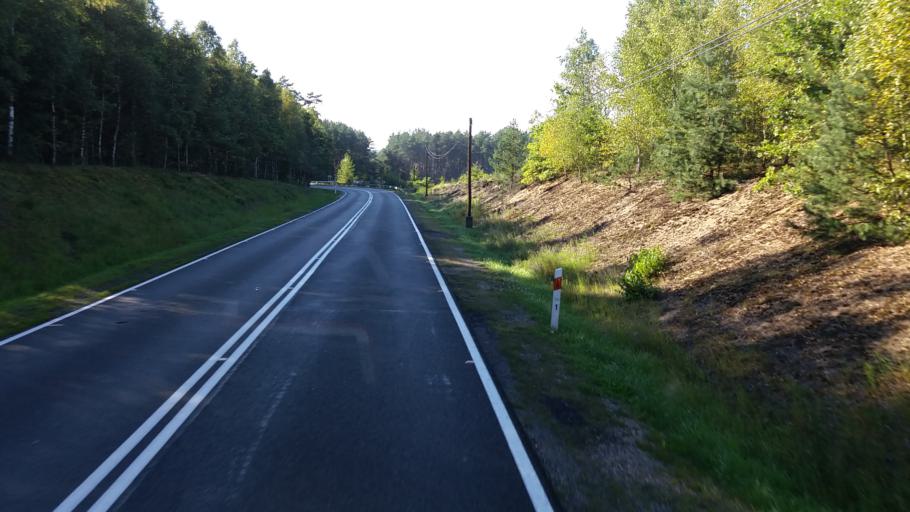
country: PL
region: West Pomeranian Voivodeship
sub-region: Powiat choszczenski
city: Drawno
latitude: 53.3036
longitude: 15.7882
